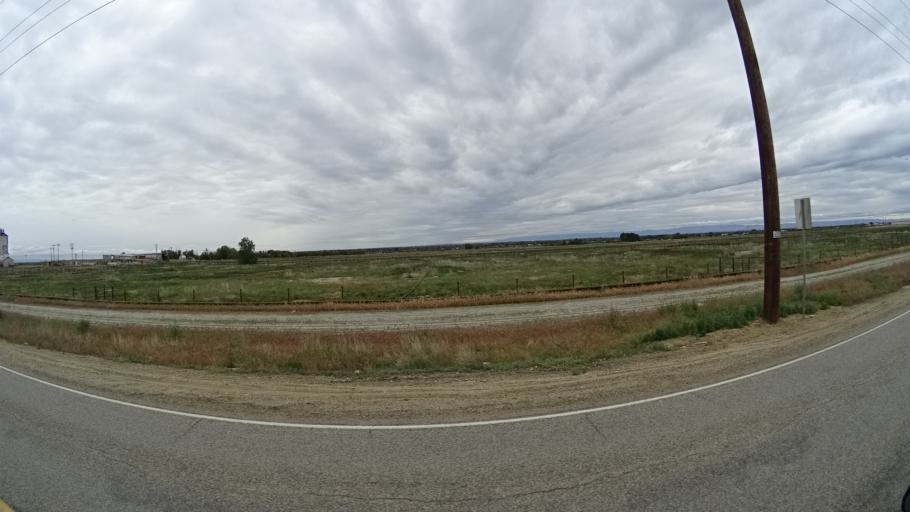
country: US
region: Idaho
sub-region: Ada County
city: Star
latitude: 43.7212
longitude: -116.4369
